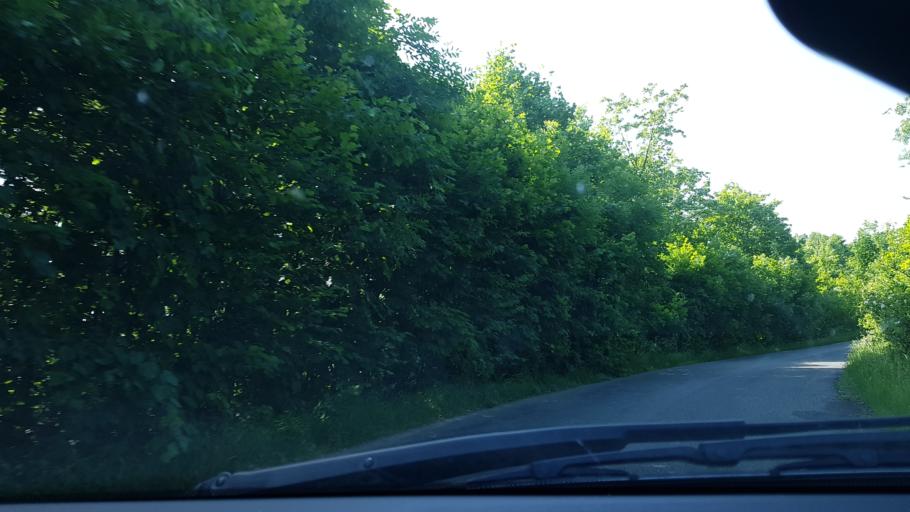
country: PL
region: Lower Silesian Voivodeship
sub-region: Powiat zabkowicki
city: Budzow
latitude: 50.5342
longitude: 16.6626
